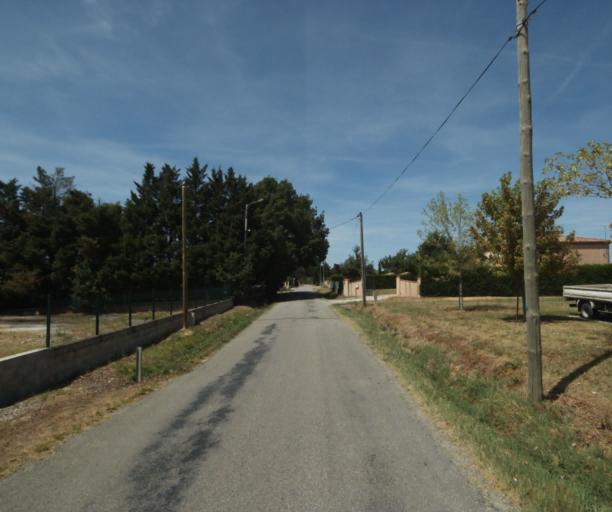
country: FR
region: Midi-Pyrenees
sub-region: Departement de la Haute-Garonne
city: Revel
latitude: 43.4854
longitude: 2.0280
